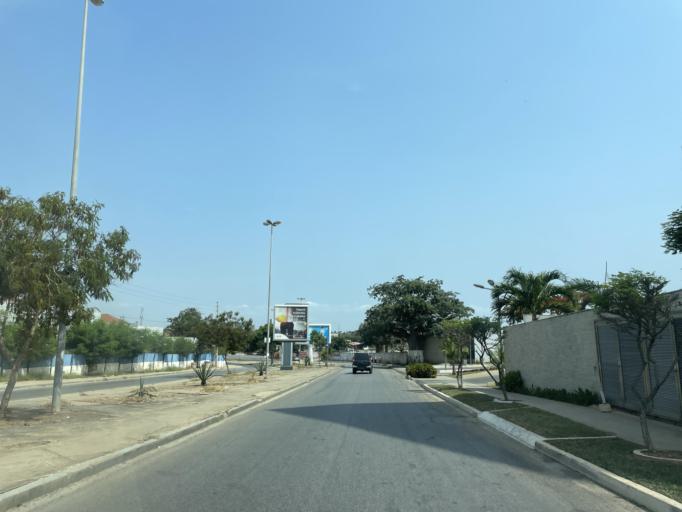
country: AO
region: Luanda
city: Luanda
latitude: -8.9256
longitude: 13.1952
